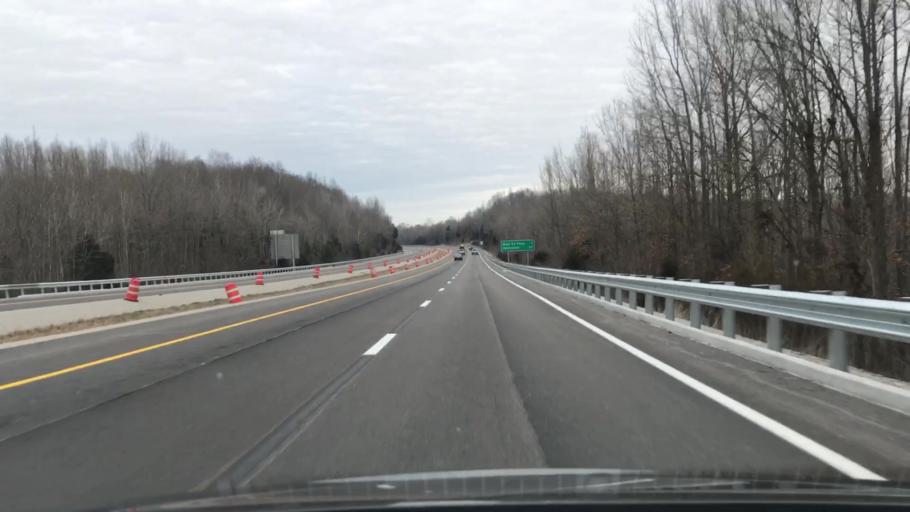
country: US
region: Kentucky
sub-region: Ohio County
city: Oak Grove
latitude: 37.3033
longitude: -86.7378
